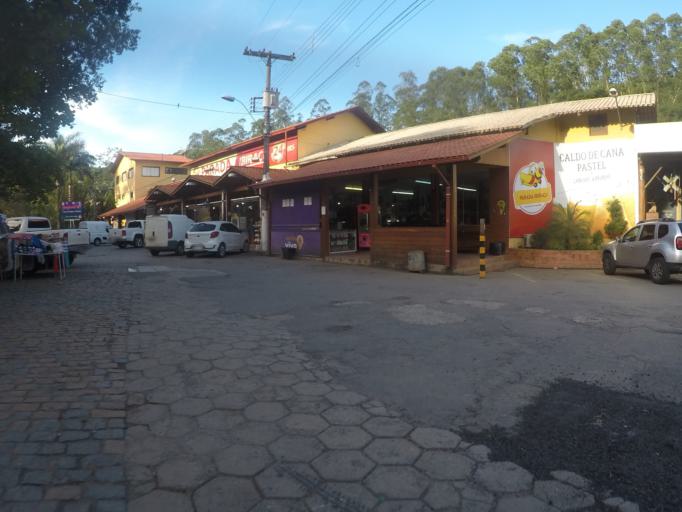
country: BR
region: Espirito Santo
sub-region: Ibiracu
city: Ibiracu
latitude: -19.8313
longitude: -40.3797
